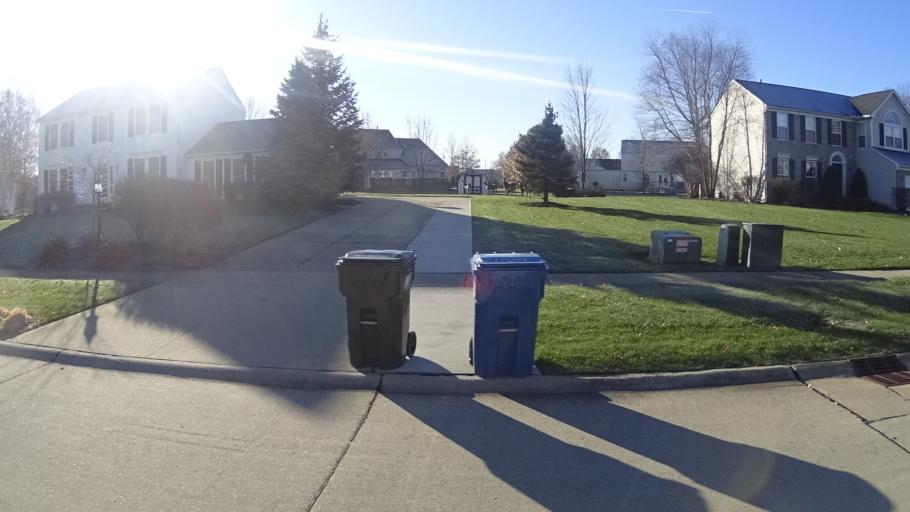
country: US
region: Ohio
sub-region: Lorain County
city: Sheffield Lake
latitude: 41.4581
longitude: -82.0785
